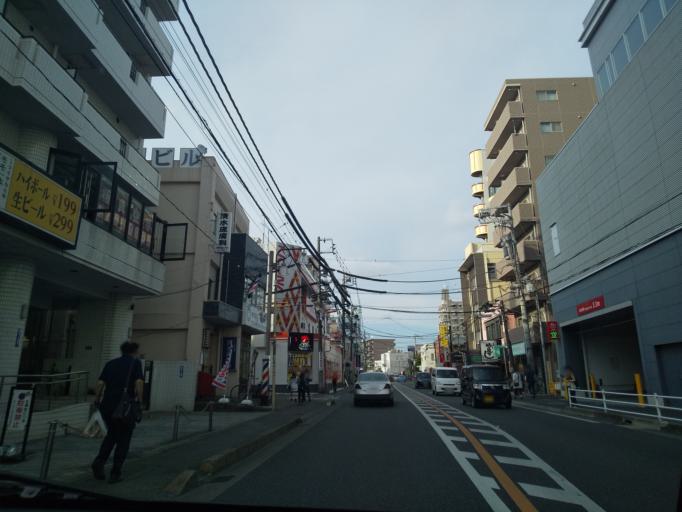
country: JP
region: Kanagawa
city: Zama
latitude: 35.4996
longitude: 139.4080
